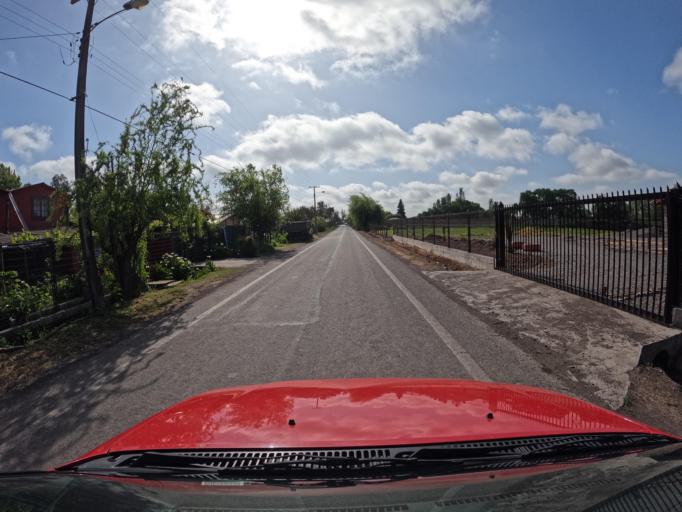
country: CL
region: Maule
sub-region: Provincia de Curico
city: Rauco
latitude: -34.8871
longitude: -71.2625
